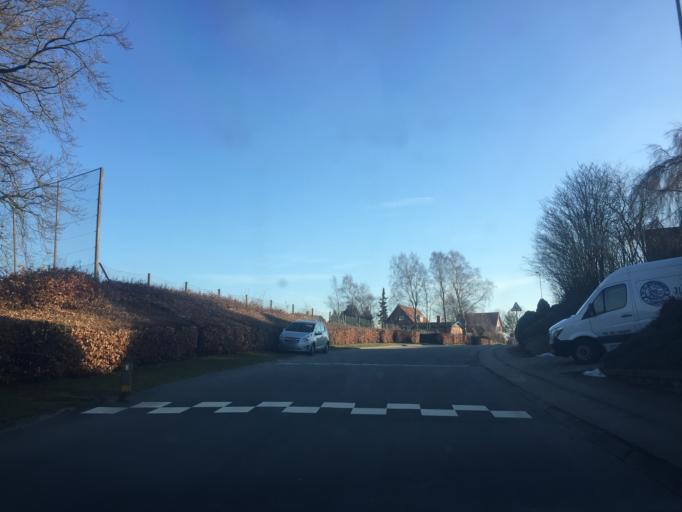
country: DK
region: South Denmark
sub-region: Nordfyns Kommune
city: Sonderso
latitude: 55.4454
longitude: 10.1926
